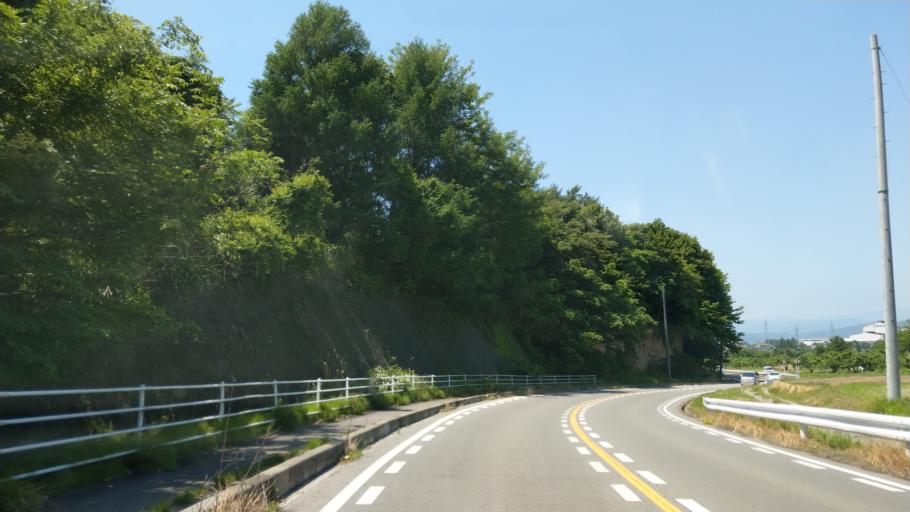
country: JP
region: Nagano
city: Komoro
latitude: 36.2963
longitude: 138.4470
